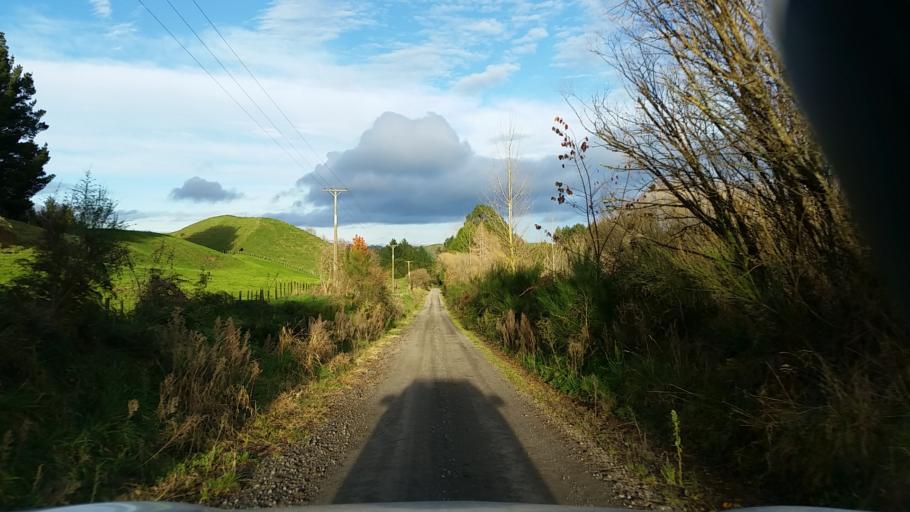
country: NZ
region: Bay of Plenty
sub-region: Rotorua District
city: Rotorua
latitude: -38.2987
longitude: 176.2764
